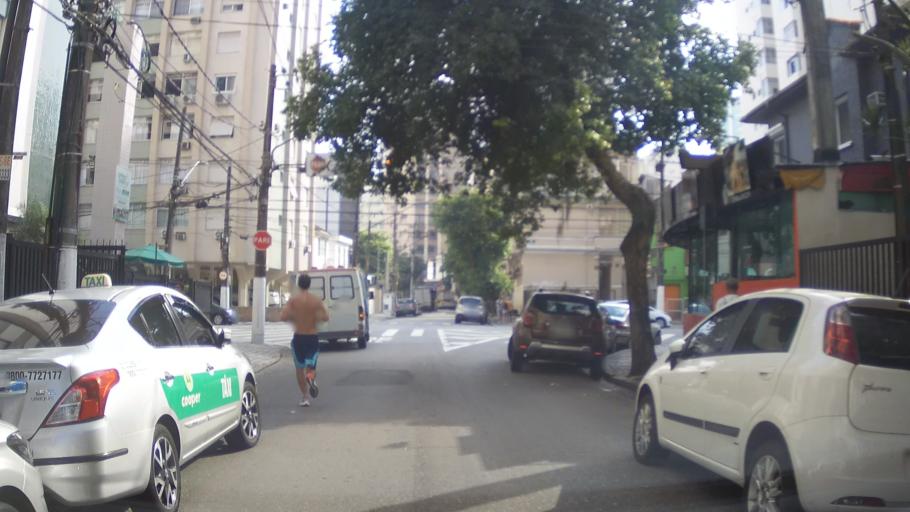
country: BR
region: Sao Paulo
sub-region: Santos
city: Santos
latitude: -23.9693
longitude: -46.3272
